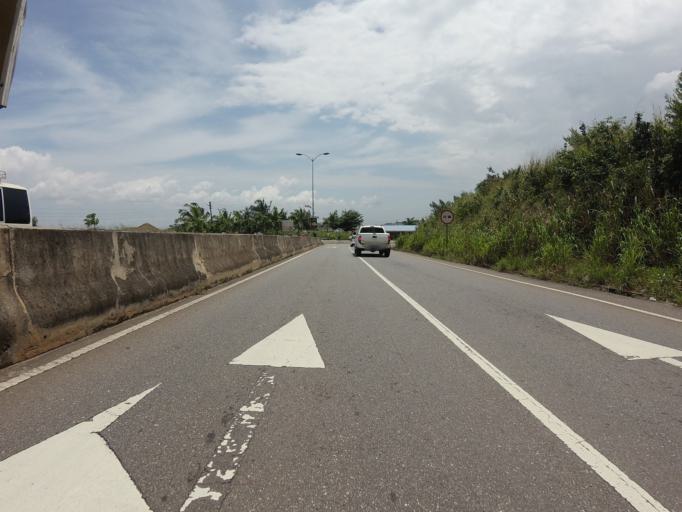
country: GH
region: Eastern
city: Aburi
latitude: 5.8019
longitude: -0.1821
